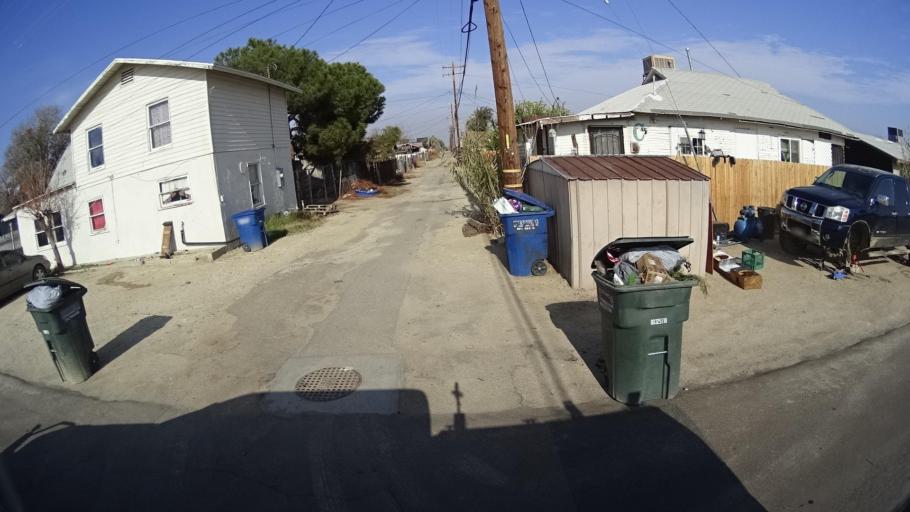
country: US
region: California
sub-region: Kern County
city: Ford City
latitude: 35.1545
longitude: -119.4640
